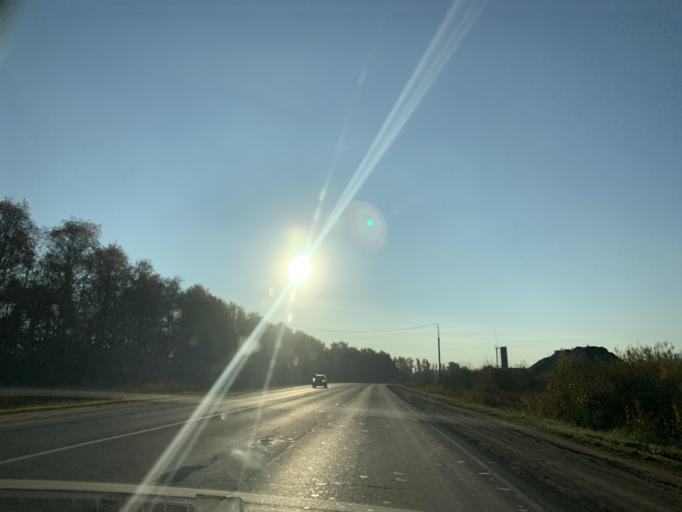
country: RU
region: Jaroslavl
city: Konstantinovskiy
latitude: 57.7409
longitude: 39.7257
